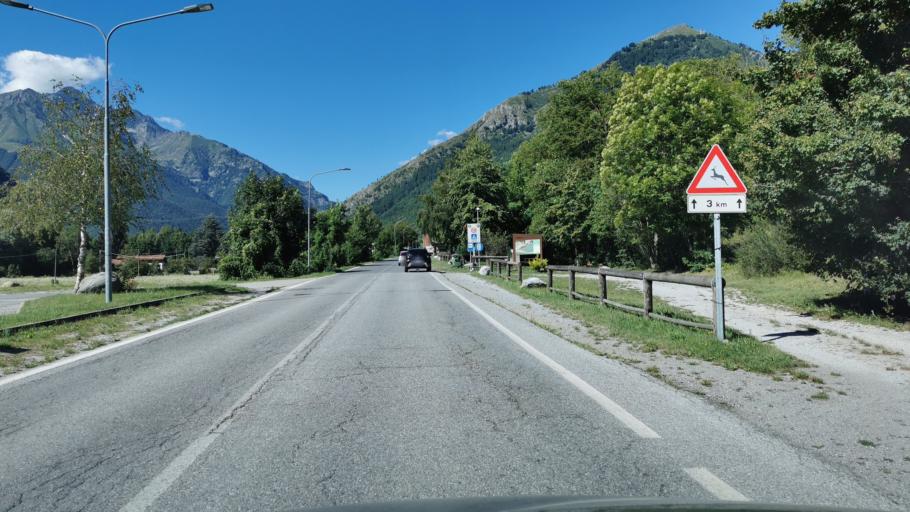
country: IT
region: Piedmont
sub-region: Provincia di Cuneo
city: Valdieri
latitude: 44.2802
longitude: 7.4064
